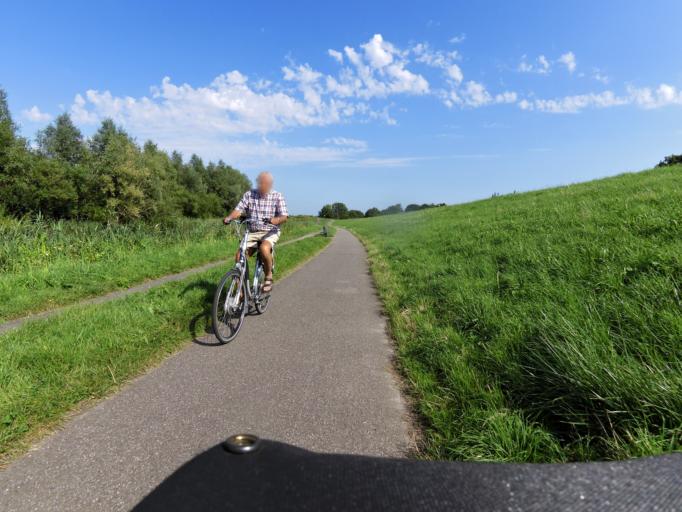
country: NL
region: South Holland
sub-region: Gemeente Oud-Beijerland
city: Oud-Beijerland
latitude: 51.8285
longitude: 4.4210
